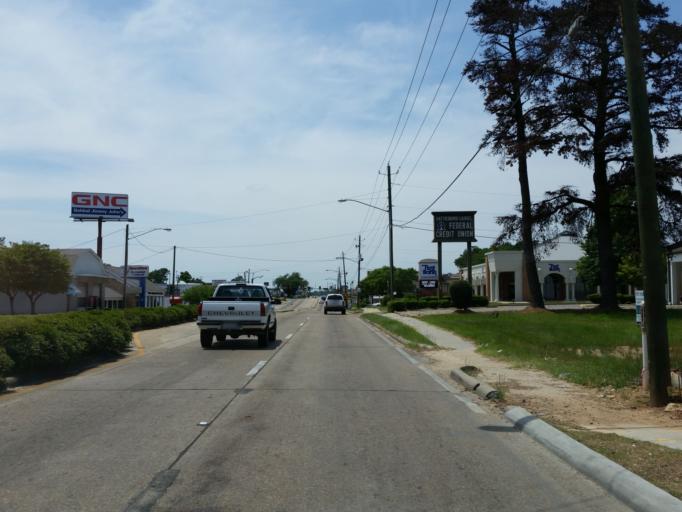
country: US
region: Mississippi
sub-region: Lamar County
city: Arnold Line
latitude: 31.3249
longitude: -89.3377
